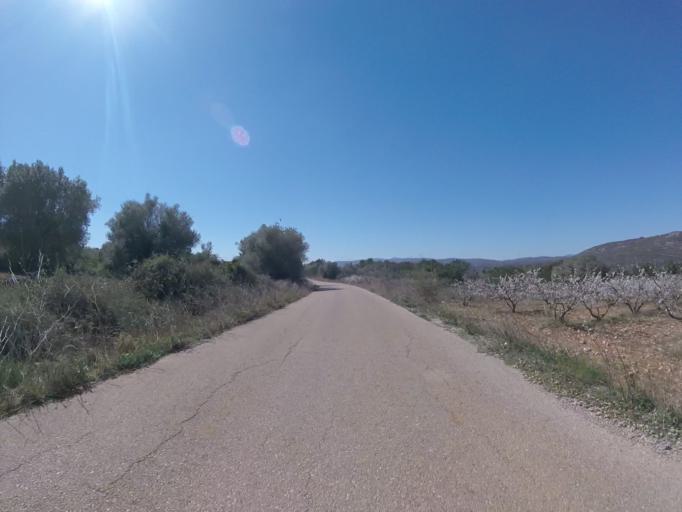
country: ES
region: Valencia
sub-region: Provincia de Castello
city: Cuevas de Vinroma
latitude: 40.3961
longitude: 0.1641
